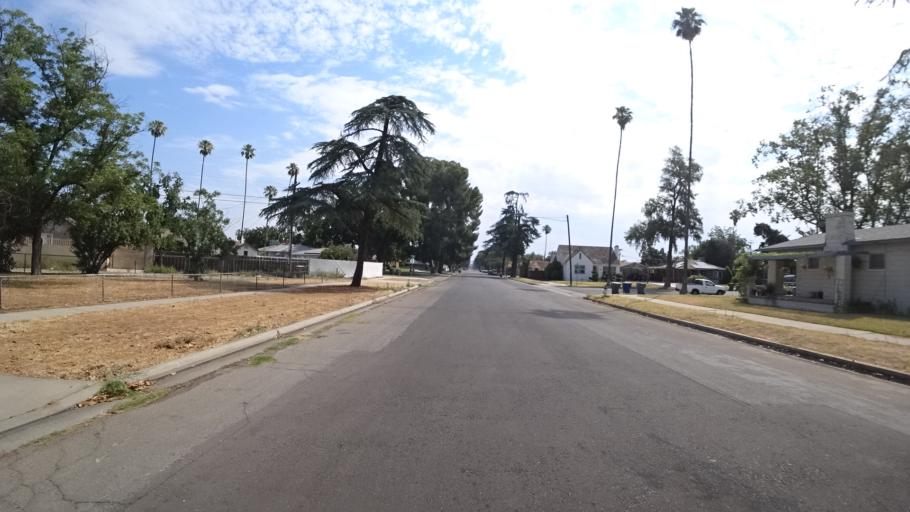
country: US
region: California
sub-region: Fresno County
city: Fresno
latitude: 36.7268
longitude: -119.8078
